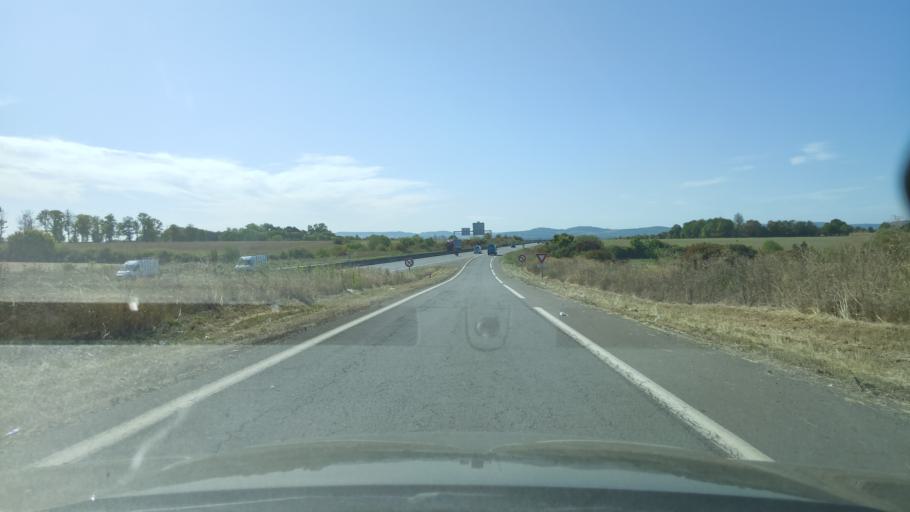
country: FR
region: Lorraine
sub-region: Departement de la Moselle
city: Peltre
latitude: 49.0895
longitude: 6.2249
